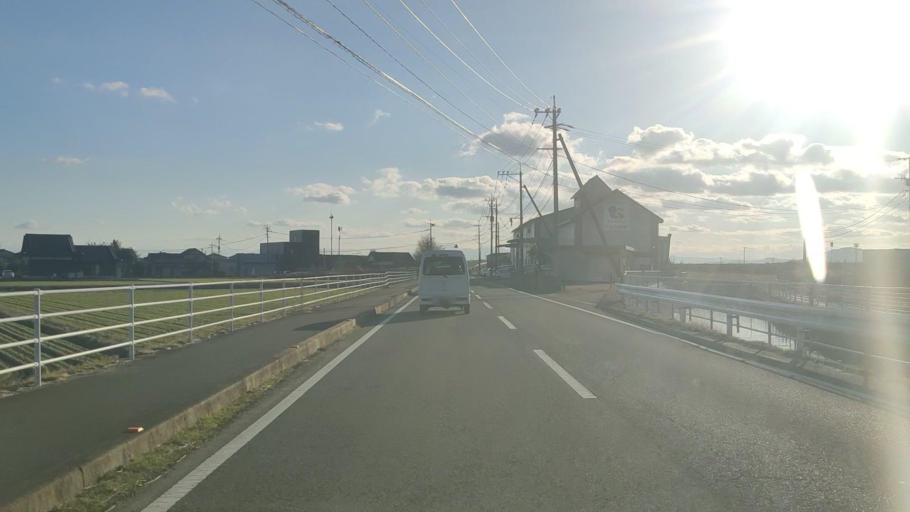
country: JP
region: Saga Prefecture
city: Saga-shi
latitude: 33.2863
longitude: 130.2330
